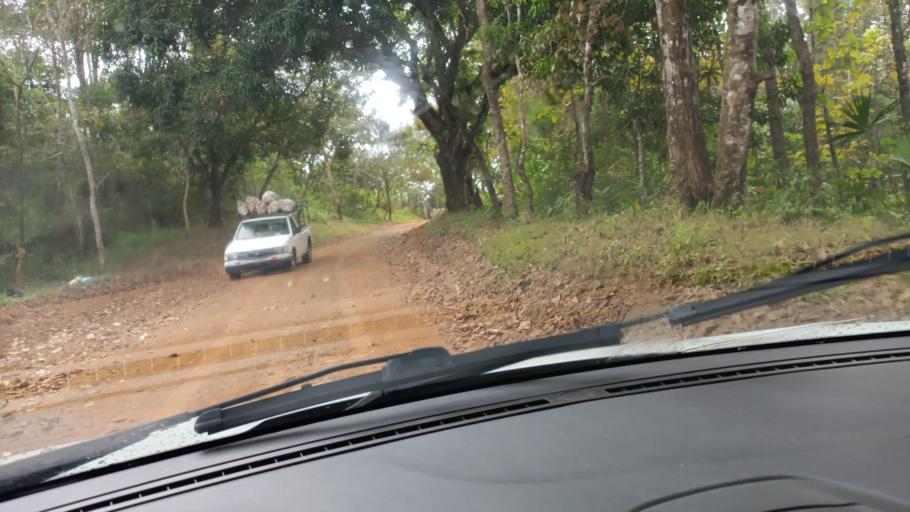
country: PA
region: Panama
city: La Cabima
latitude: 9.1289
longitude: -79.5107
